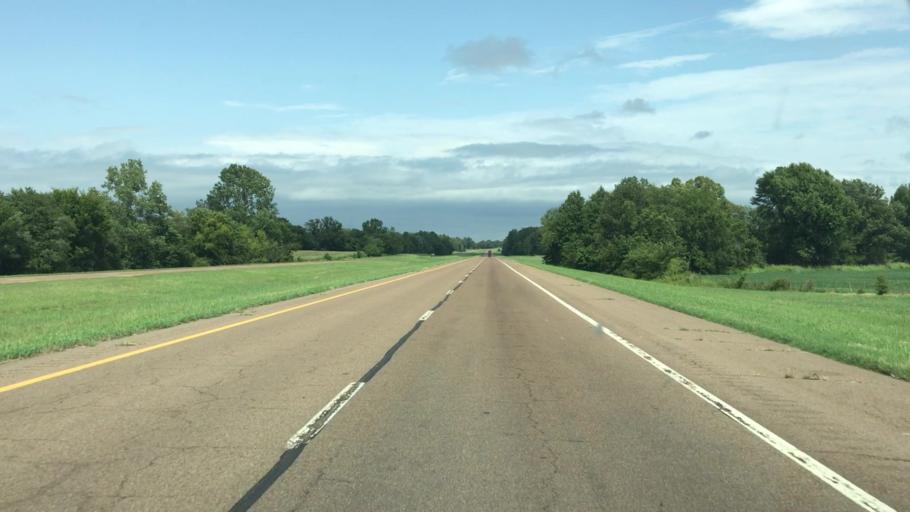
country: US
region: Tennessee
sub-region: Obion County
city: Union City
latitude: 36.4663
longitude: -88.9746
